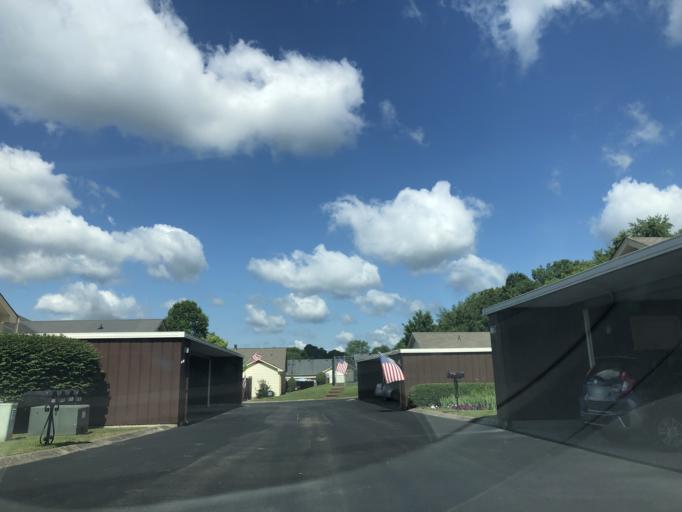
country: US
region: Tennessee
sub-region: Davidson County
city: Belle Meade
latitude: 36.0654
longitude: -86.9464
